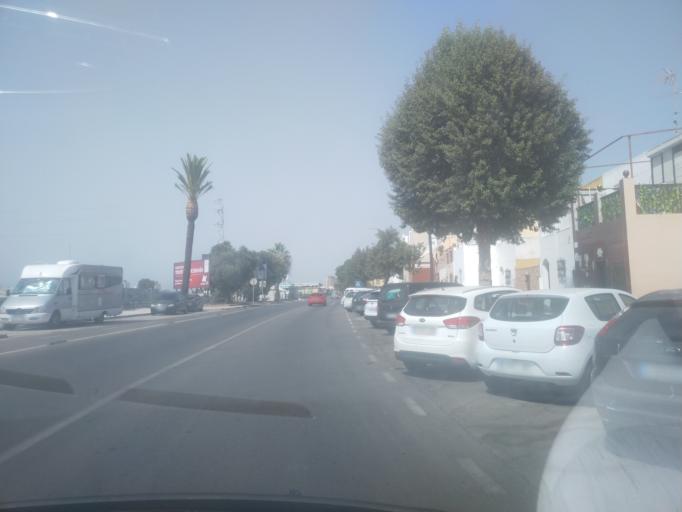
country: ES
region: Andalusia
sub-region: Provincia de Cadiz
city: San Fernando
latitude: 36.4700
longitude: -6.2047
